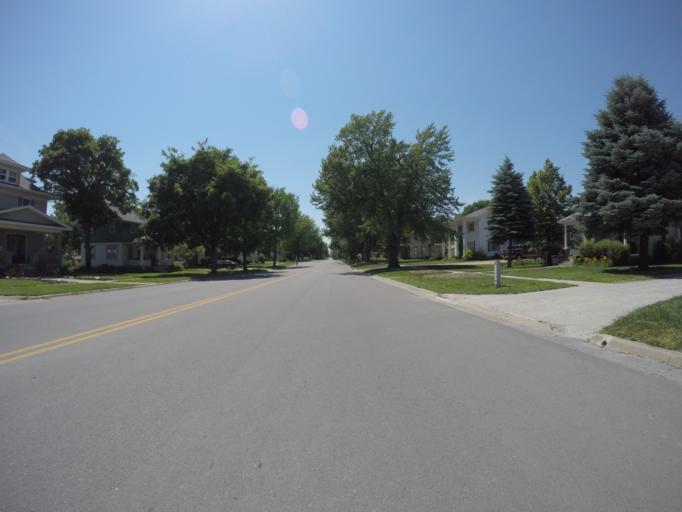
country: US
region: Kansas
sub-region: Nemaha County
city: Sabetha
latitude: 39.9034
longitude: -95.7921
